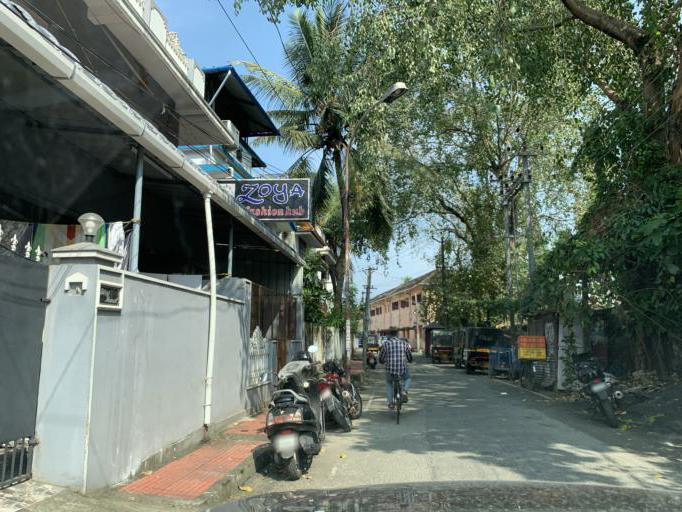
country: IN
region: Kerala
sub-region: Ernakulam
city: Cochin
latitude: 9.9611
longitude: 76.2536
